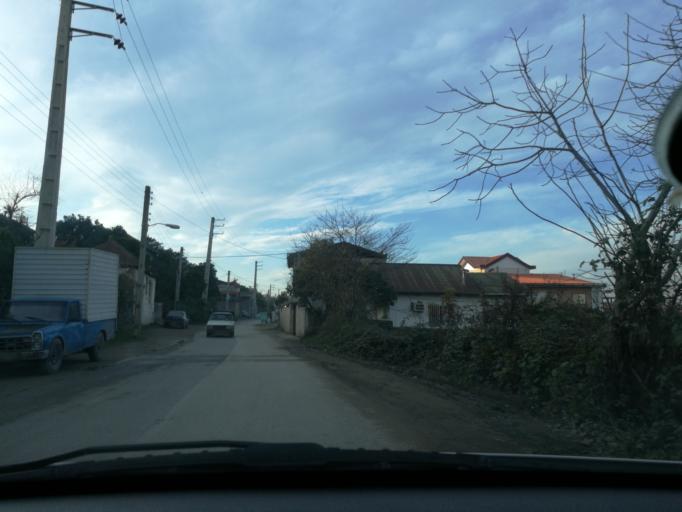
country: IR
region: Mazandaran
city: Chalus
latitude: 36.6410
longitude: 51.4417
